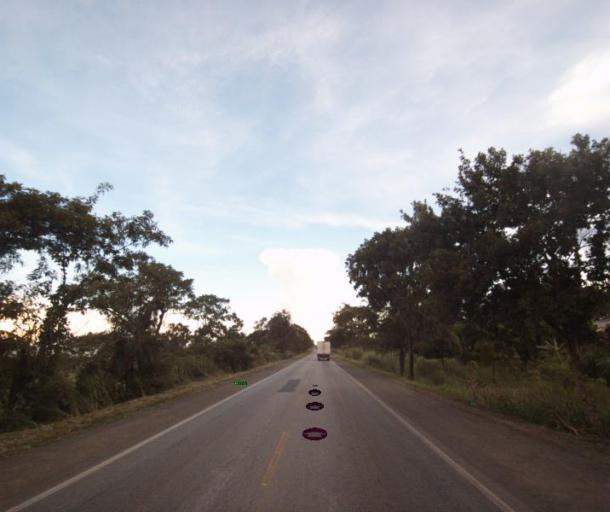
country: BR
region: Goias
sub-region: Uruacu
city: Uruacu
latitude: -14.3276
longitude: -49.1530
